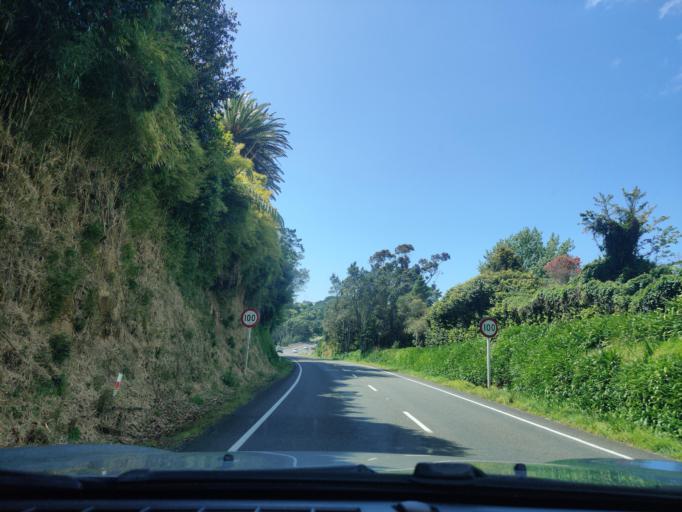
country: NZ
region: Taranaki
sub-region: New Plymouth District
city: New Plymouth
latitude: -39.1144
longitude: 173.9579
